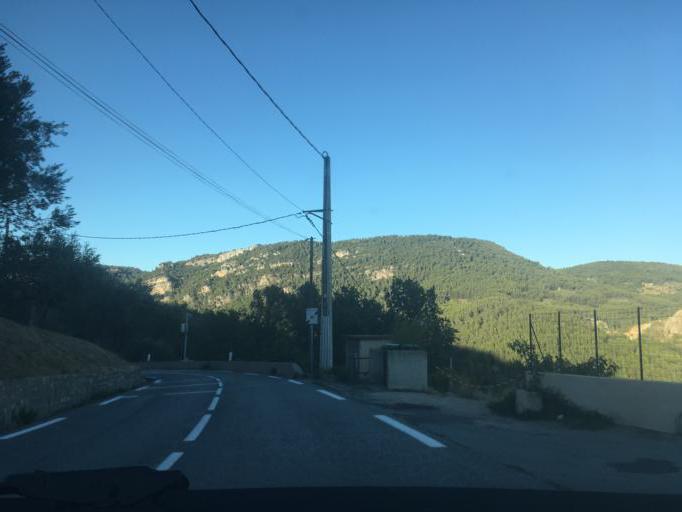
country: FR
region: Provence-Alpes-Cote d'Azur
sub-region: Departement du Var
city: Flayosc
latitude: 43.5662
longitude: 6.4150
